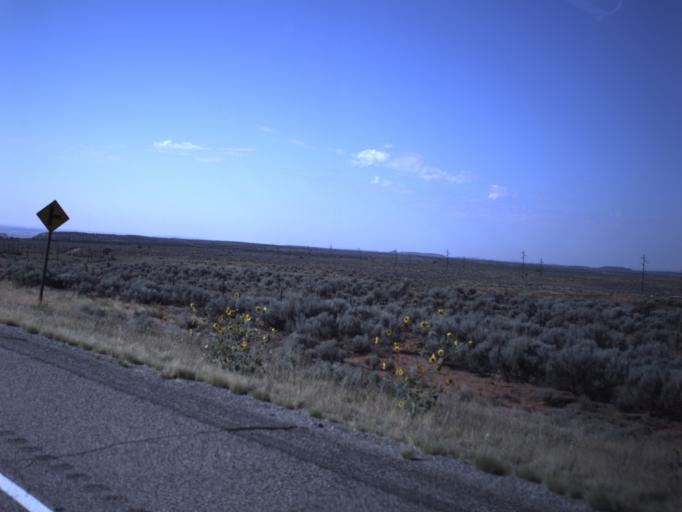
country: US
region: Utah
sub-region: San Juan County
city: Blanding
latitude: 37.5157
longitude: -109.4941
